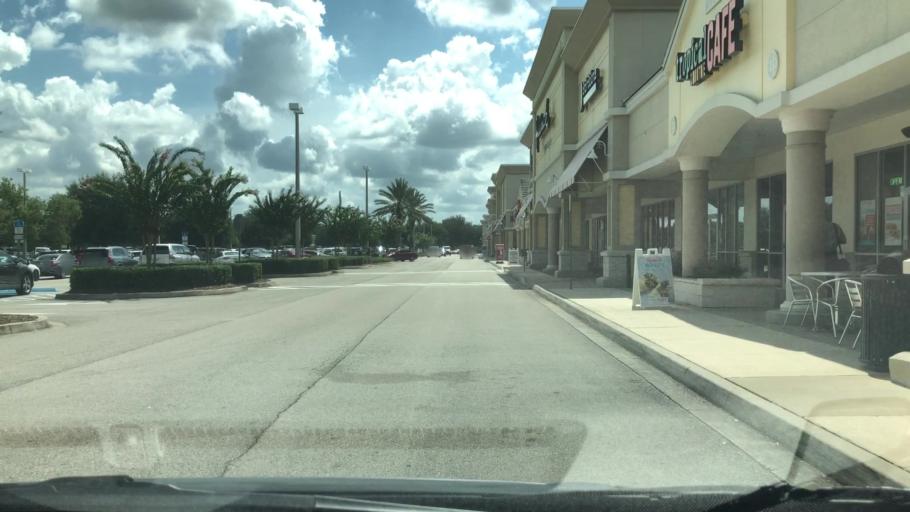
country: US
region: Florida
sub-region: Saint Johns County
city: Fruit Cove
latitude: 30.1410
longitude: -81.5508
